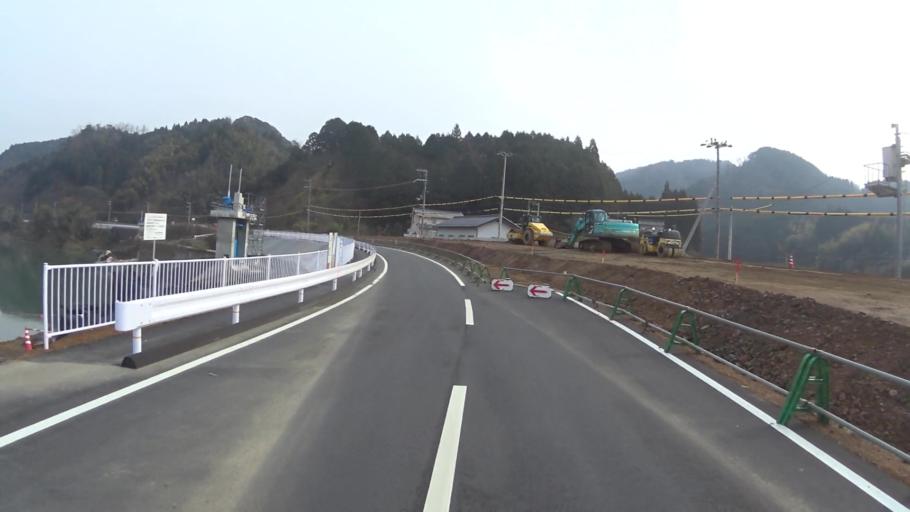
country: JP
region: Kyoto
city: Fukuchiyama
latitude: 35.3891
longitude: 135.1825
